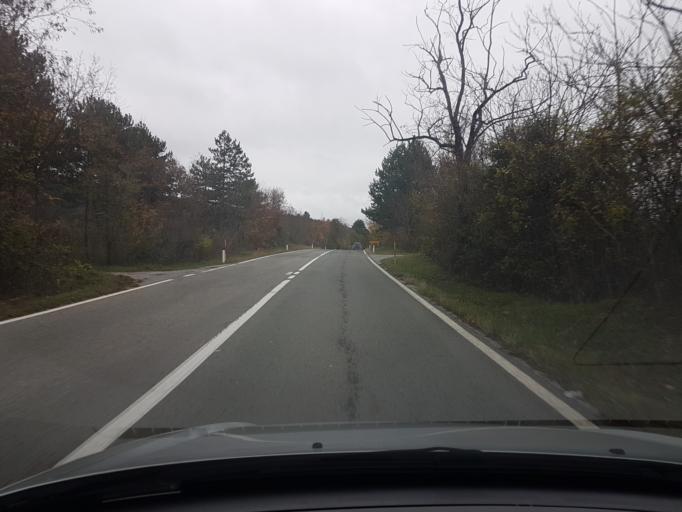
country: SI
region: Divaca
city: Divaca
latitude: 45.7358
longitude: 13.9507
